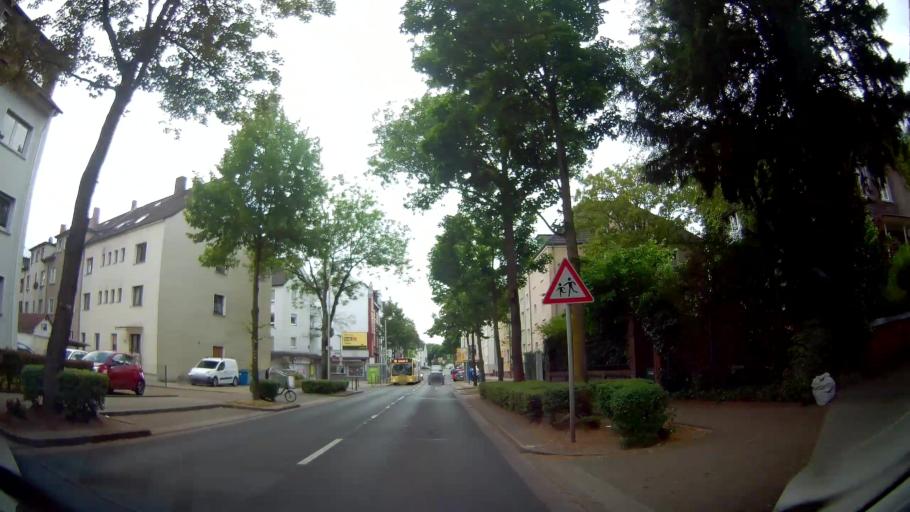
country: DE
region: North Rhine-Westphalia
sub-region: Regierungsbezirk Dusseldorf
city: Essen
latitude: 51.4946
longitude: 7.0136
